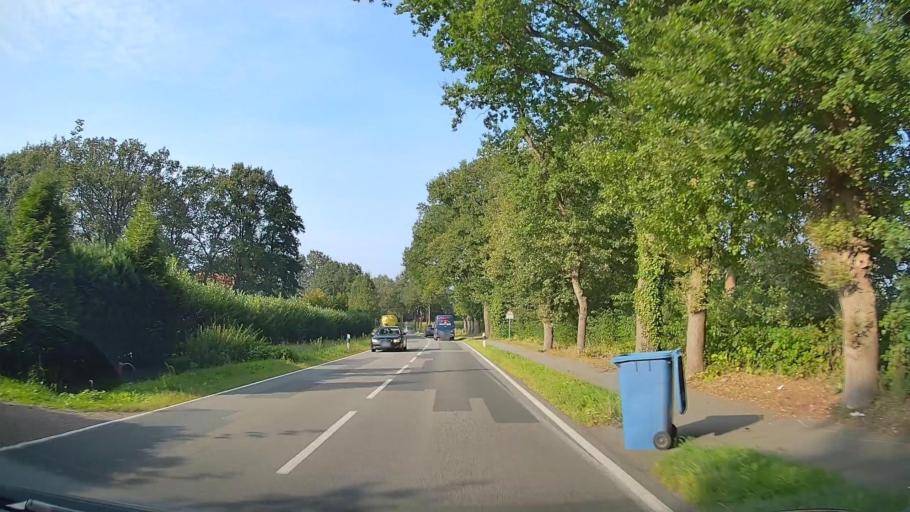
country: DE
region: Lower Saxony
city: Friesoythe
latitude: 53.0913
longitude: 7.8340
